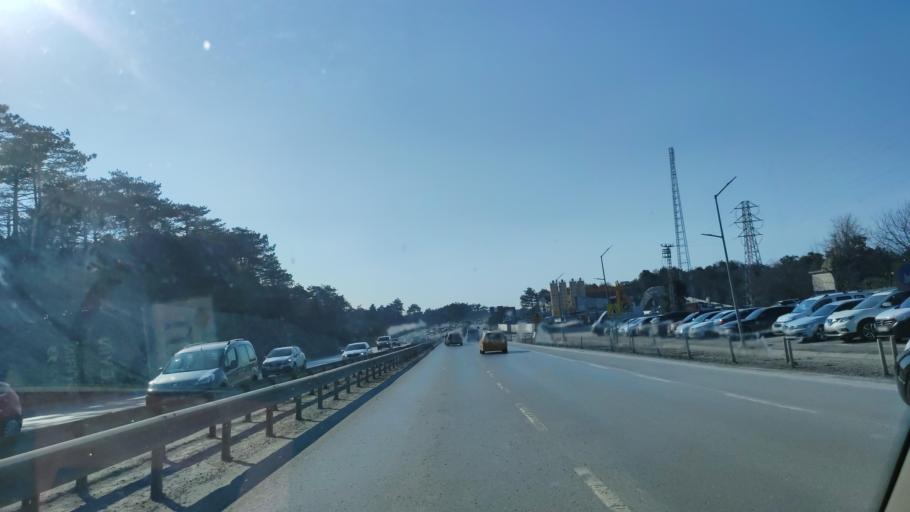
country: TR
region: Istanbul
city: Basaksehir
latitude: 41.1603
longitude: 28.7805
